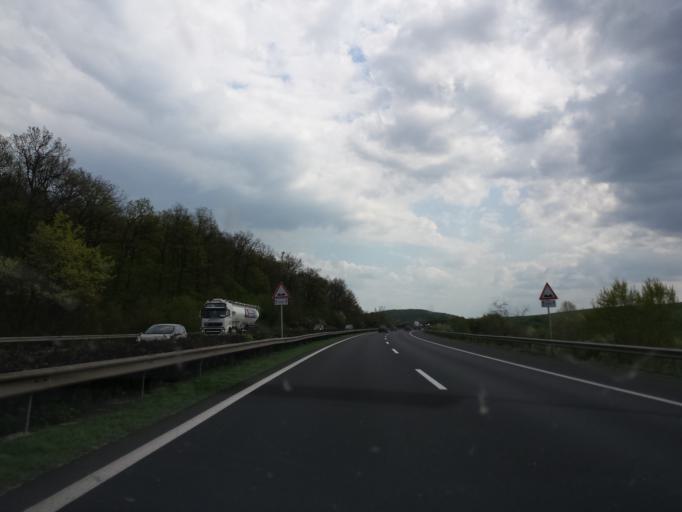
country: HU
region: Komarom-Esztergom
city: Tarjan
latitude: 47.5692
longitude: 18.4765
